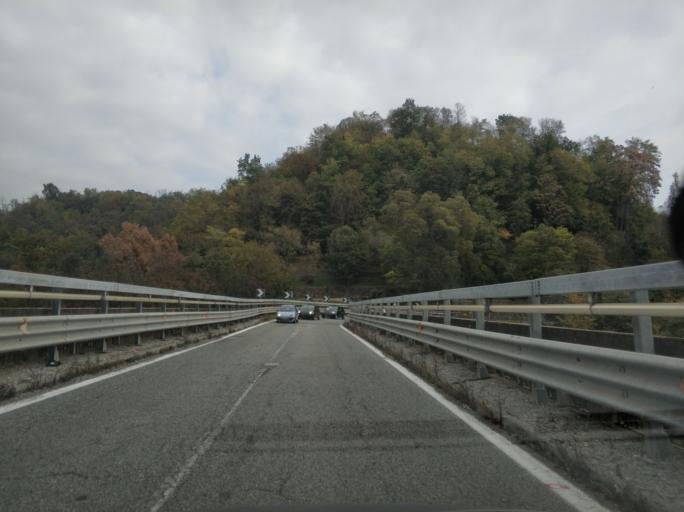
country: IT
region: Piedmont
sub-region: Provincia di Torino
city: Baldissero Canavese
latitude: 45.4147
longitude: 7.7545
